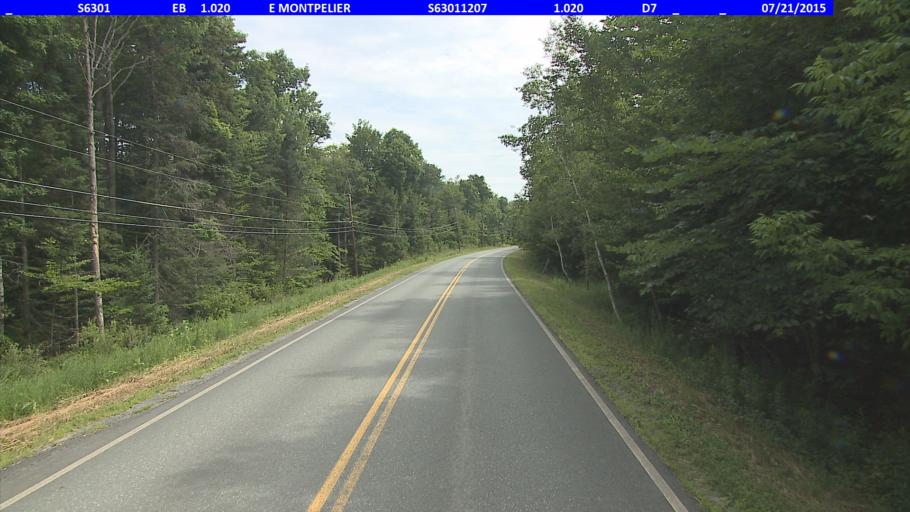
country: US
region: Vermont
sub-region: Washington County
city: Montpelier
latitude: 44.2803
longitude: -72.5363
